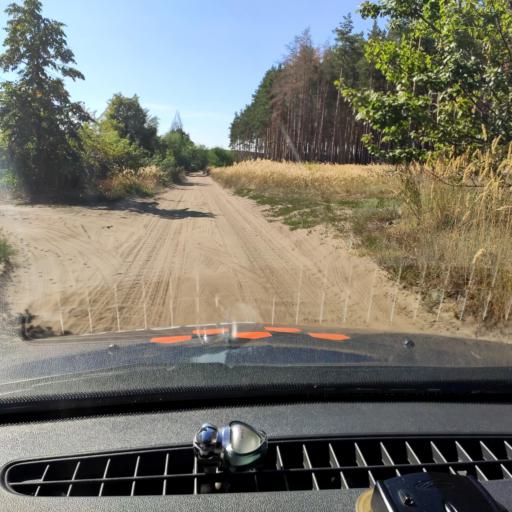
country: RU
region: Voronezj
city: Shilovo
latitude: 51.5324
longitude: 39.1616
